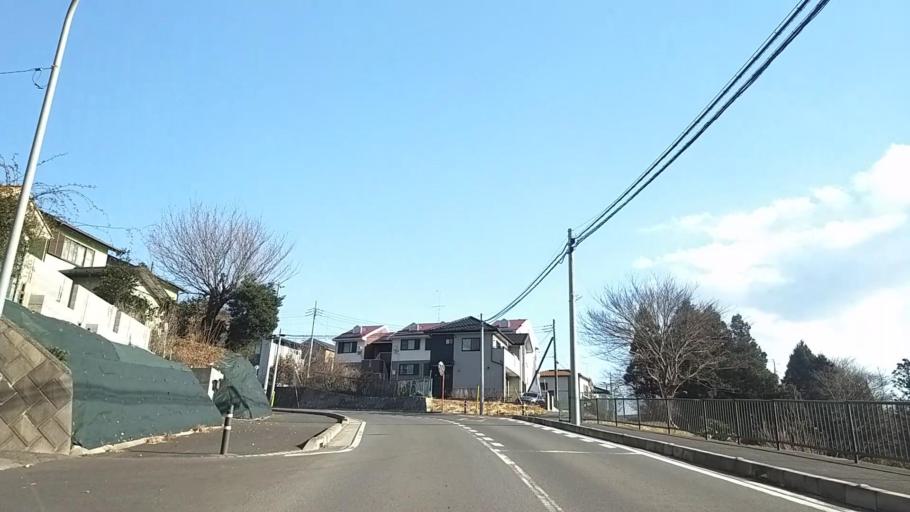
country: JP
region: Kanagawa
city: Atsugi
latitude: 35.4564
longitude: 139.3249
